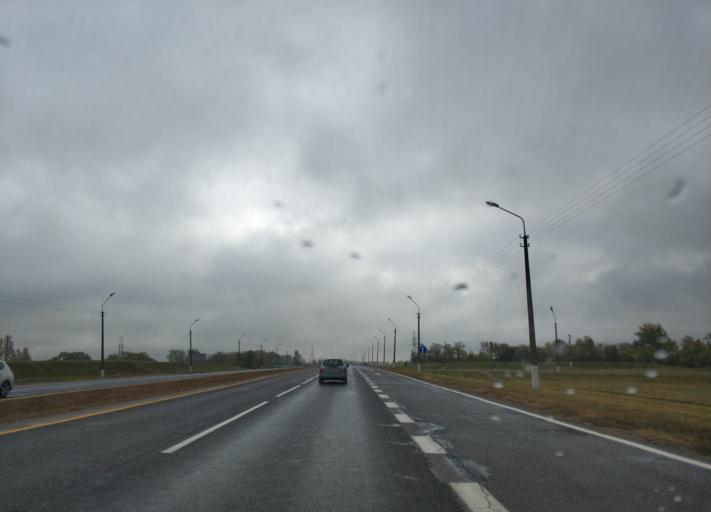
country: BY
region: Vitebsk
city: Vitebsk
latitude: 55.1927
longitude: 30.1233
